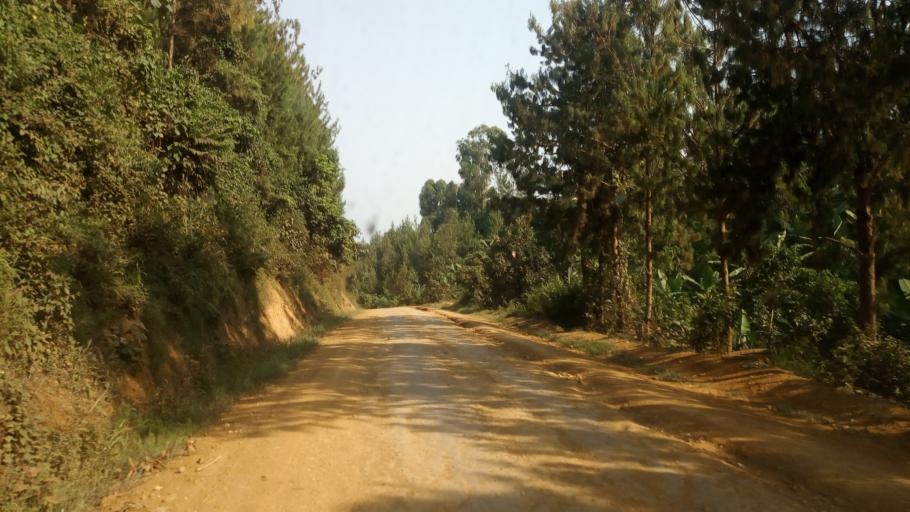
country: UG
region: Western Region
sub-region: Kanungu District
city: Ntungamo
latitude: -0.8278
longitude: 29.7070
